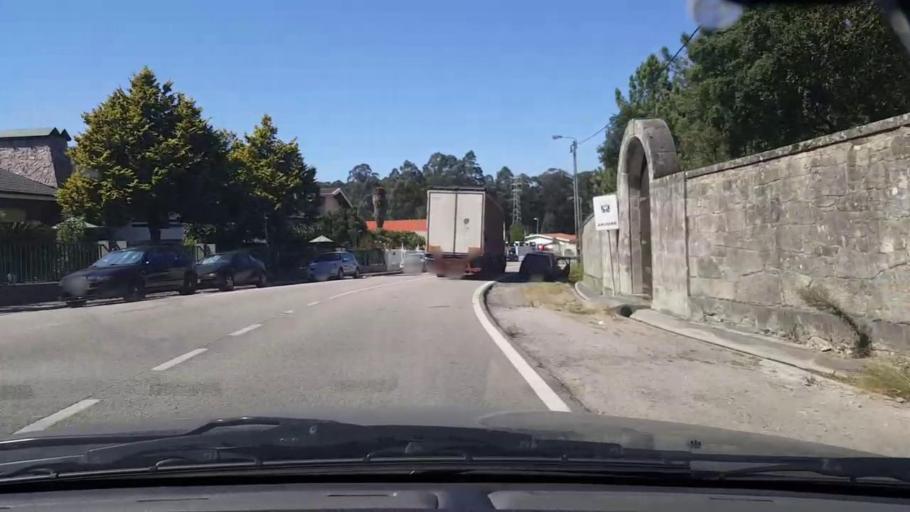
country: PT
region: Porto
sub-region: Vila do Conde
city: Arvore
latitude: 41.3381
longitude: -8.6894
